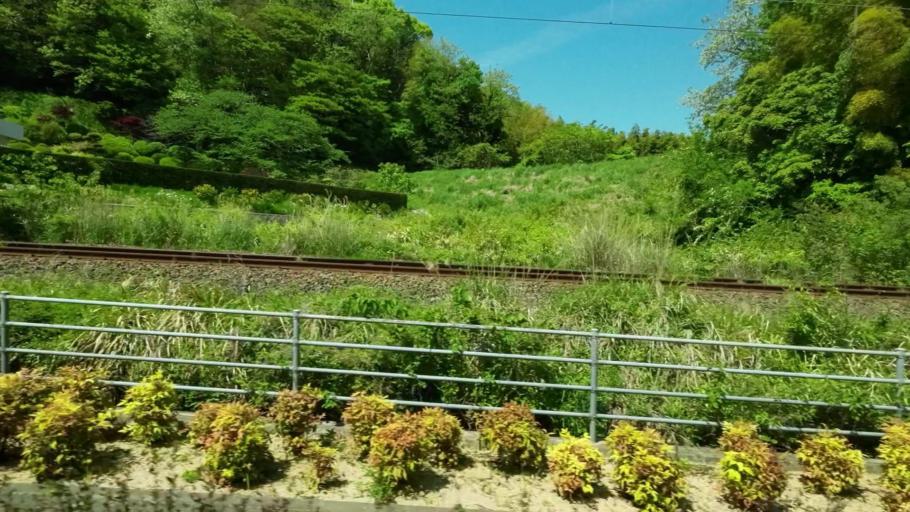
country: JP
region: Ehime
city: Hojo
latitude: 34.0754
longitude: 132.9858
